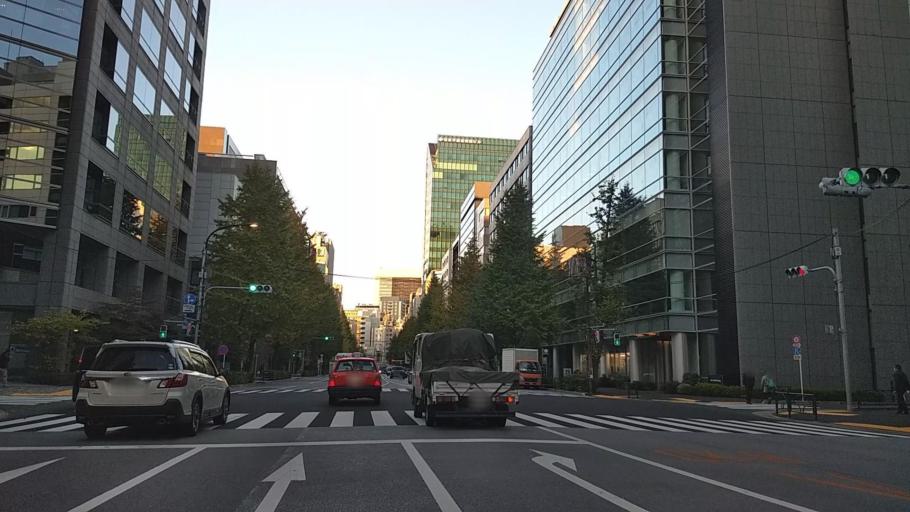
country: JP
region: Tokyo
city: Tokyo
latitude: 35.6907
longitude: 139.7646
